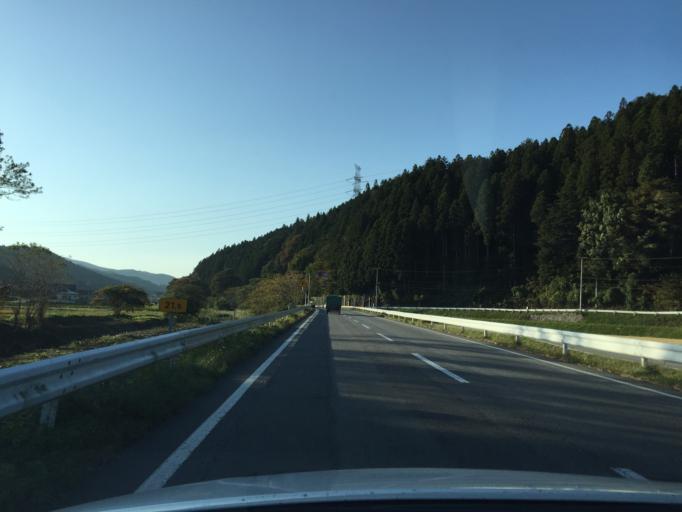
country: JP
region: Fukushima
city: Iwaki
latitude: 37.1356
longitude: 140.7081
